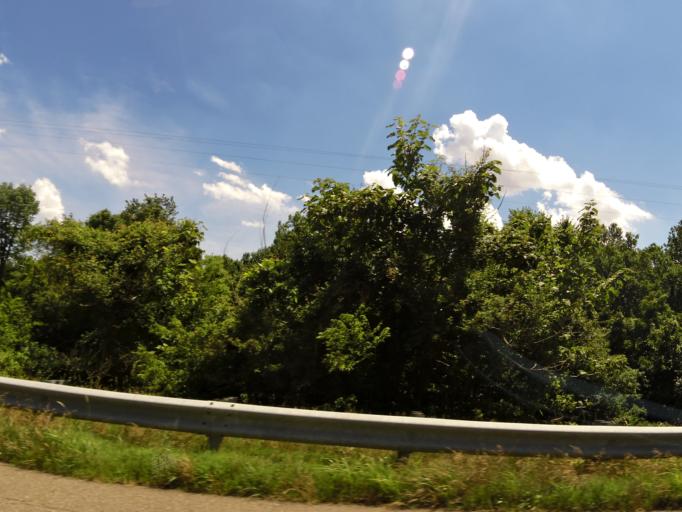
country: US
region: Tennessee
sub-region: Dyer County
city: Dyersburg
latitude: 36.0700
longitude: -89.4516
